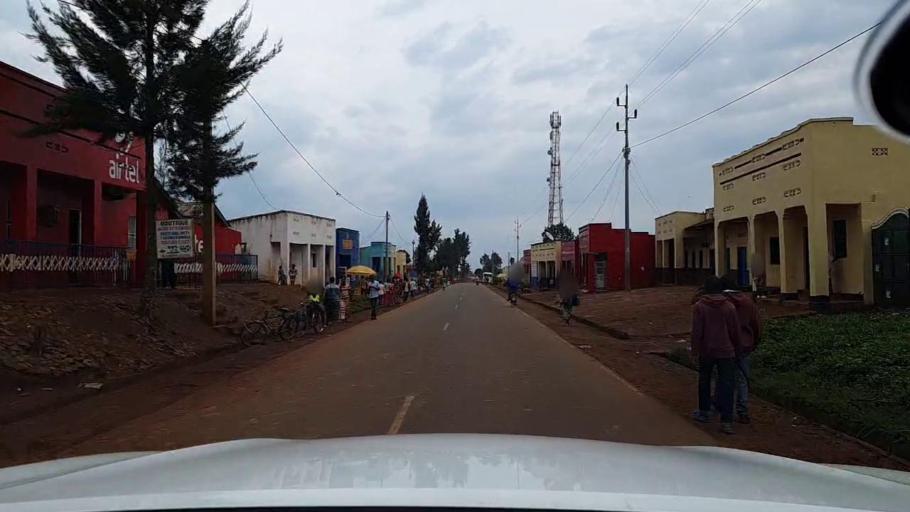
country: RW
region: Western Province
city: Cyangugu
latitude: -2.6260
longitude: 28.9495
